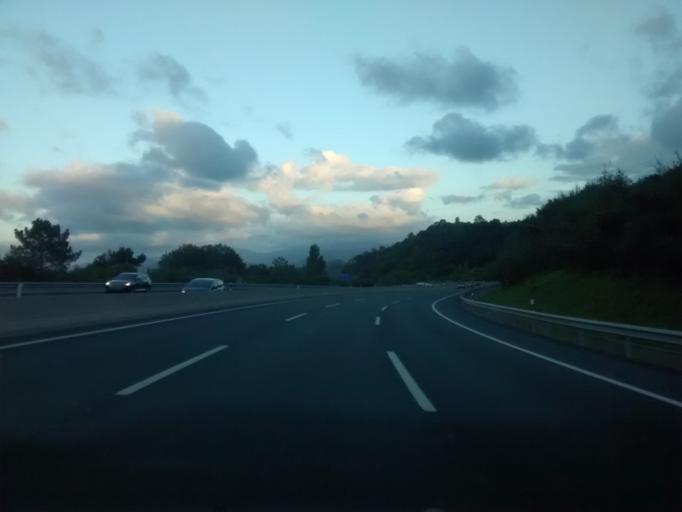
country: ES
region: Basque Country
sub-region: Provincia de Guipuzcoa
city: Usurbil
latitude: 43.2949
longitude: -2.0534
